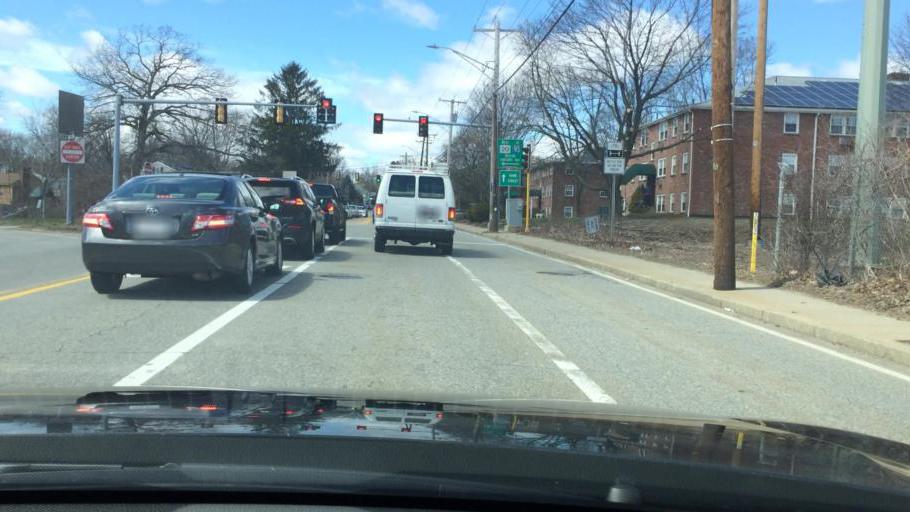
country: US
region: Massachusetts
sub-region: Essex County
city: Methuen
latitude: 42.7429
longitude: -71.1691
